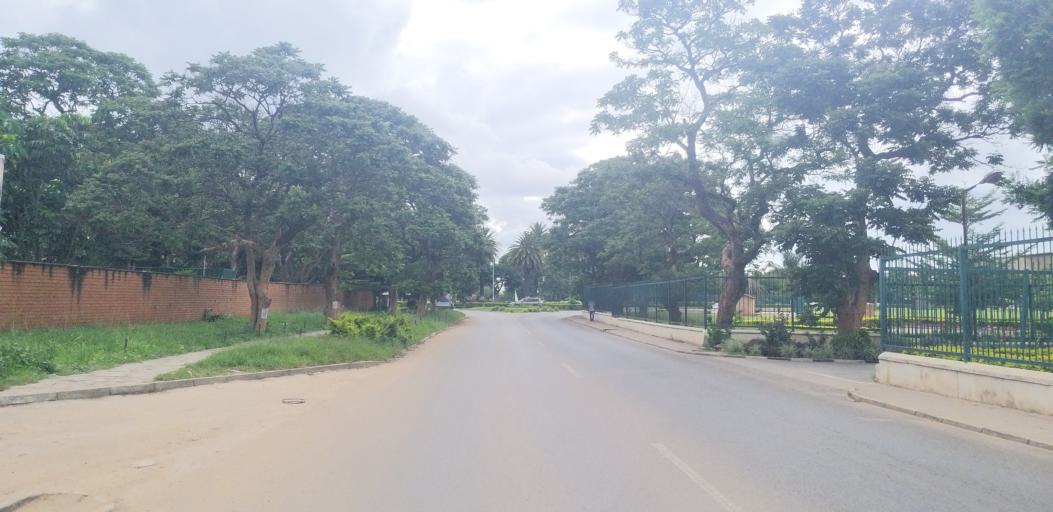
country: ZM
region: Lusaka
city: Lusaka
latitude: -15.4196
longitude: 28.3070
